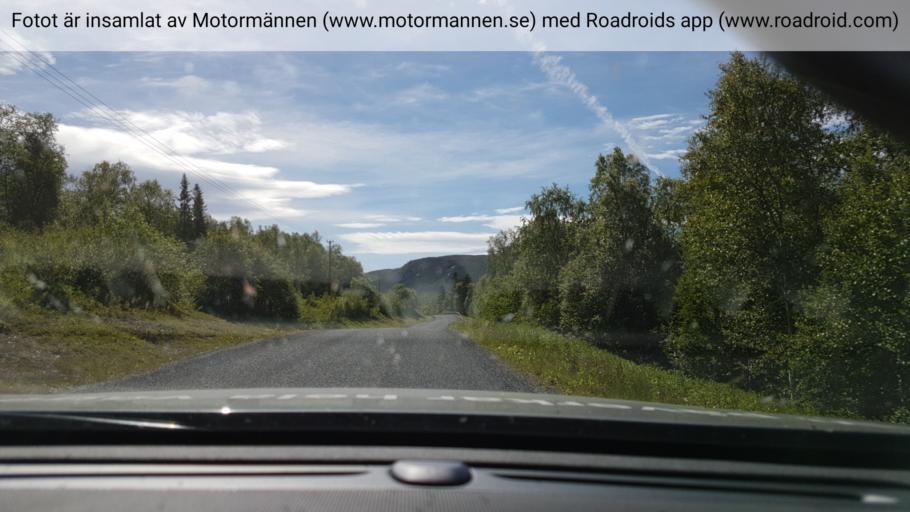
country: SE
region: Vaesterbotten
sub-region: Vilhelmina Kommun
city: Sjoberg
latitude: 65.2927
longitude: 15.2931
